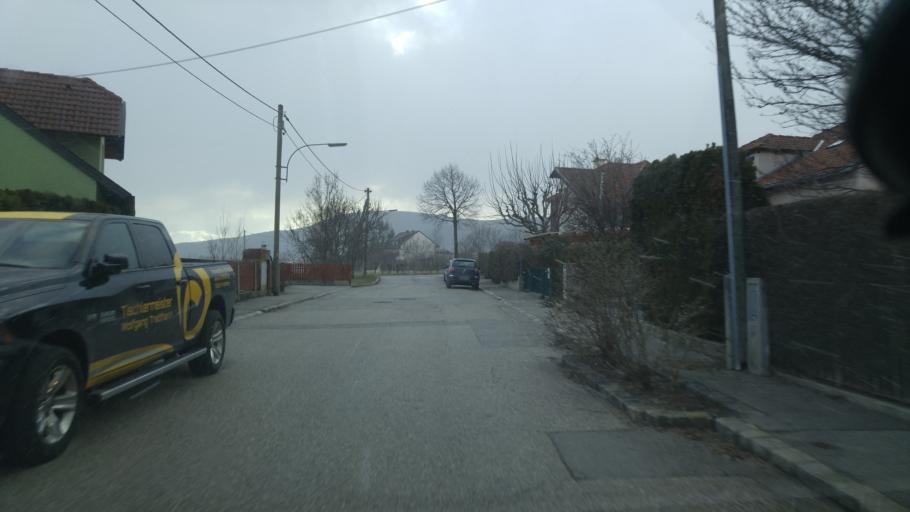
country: AT
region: Lower Austria
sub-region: Politischer Bezirk Baden
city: Baden
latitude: 47.9947
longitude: 16.2095
